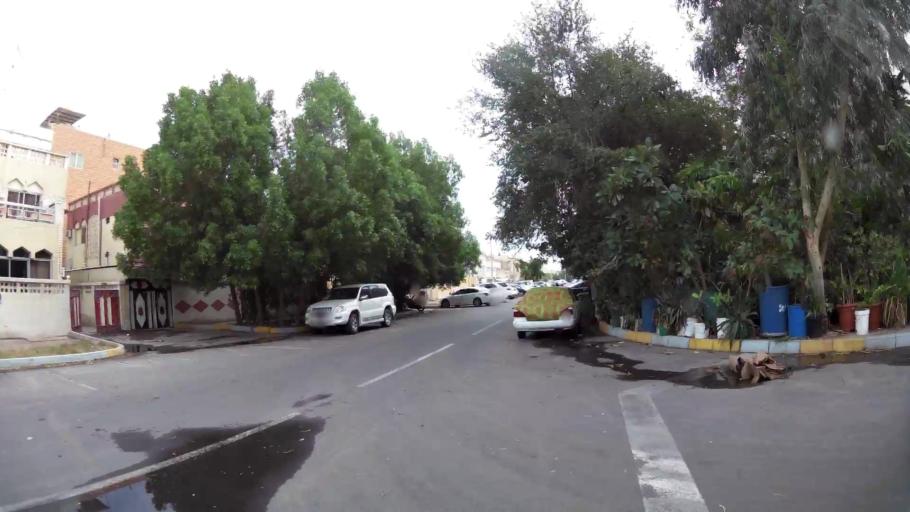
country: AE
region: Abu Dhabi
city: Abu Dhabi
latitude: 24.4381
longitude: 54.4319
